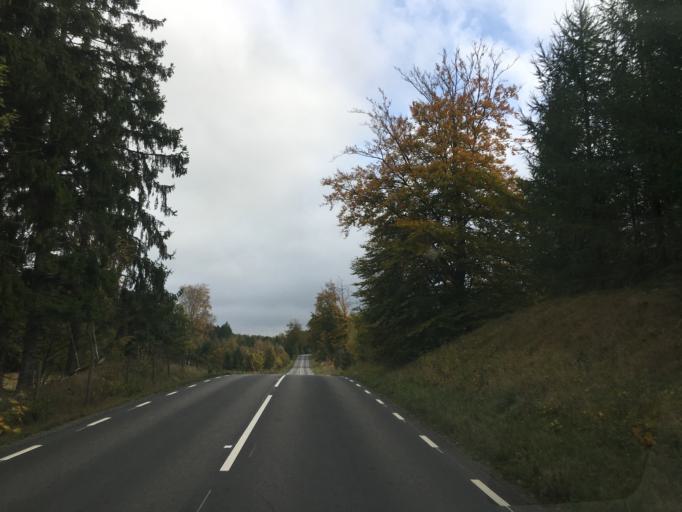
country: SE
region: Skane
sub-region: Tomelilla Kommun
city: Tomelilla
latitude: 55.6363
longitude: 14.0813
